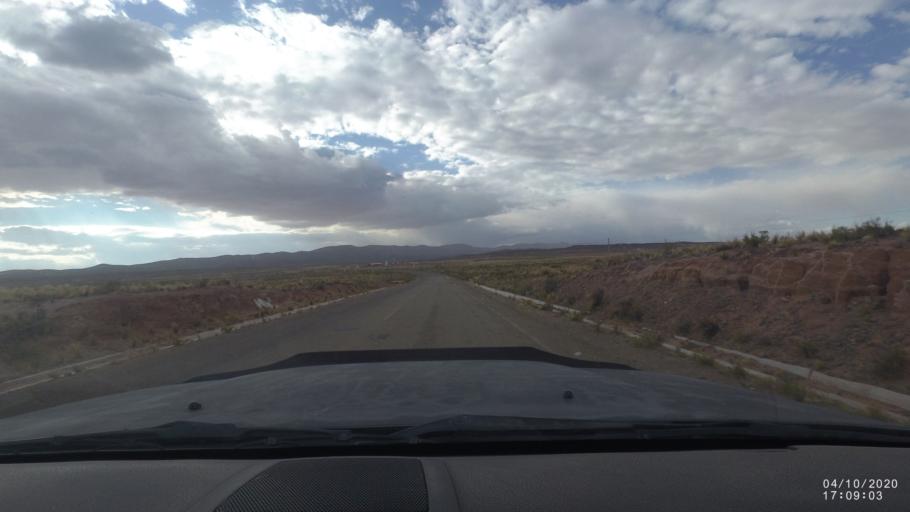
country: BO
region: Oruro
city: Oruro
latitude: -18.3425
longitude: -67.5787
